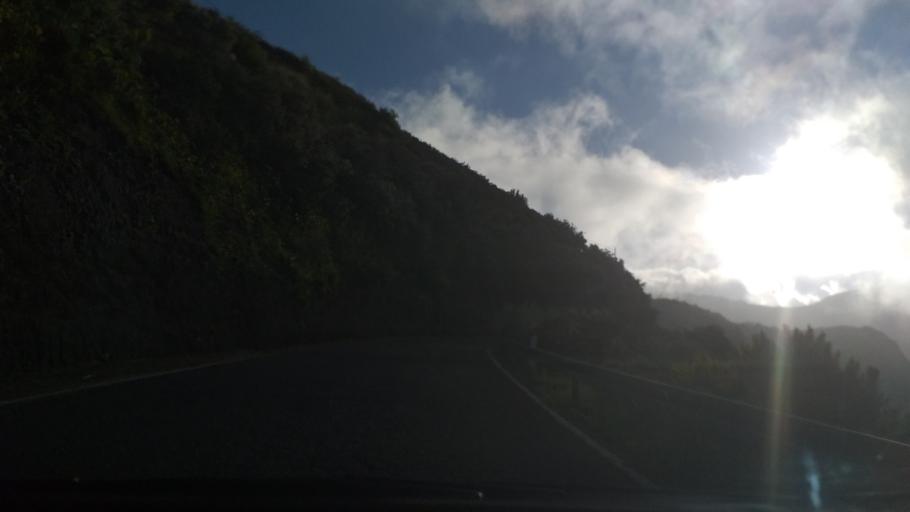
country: ES
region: Canary Islands
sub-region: Provincia de Las Palmas
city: Valsequillo de Gran Canaria
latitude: 27.9575
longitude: -15.5079
